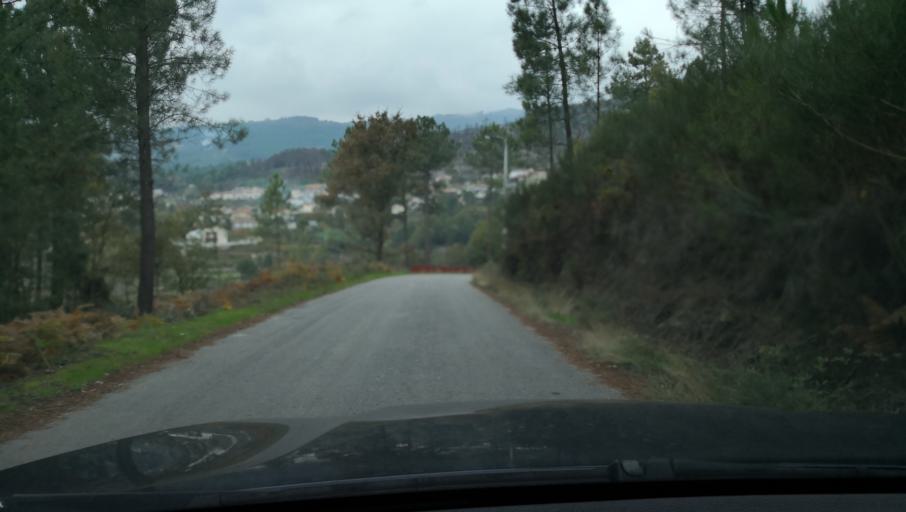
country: PT
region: Vila Real
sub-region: Vila Real
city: Vila Real
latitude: 41.3199
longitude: -7.7542
